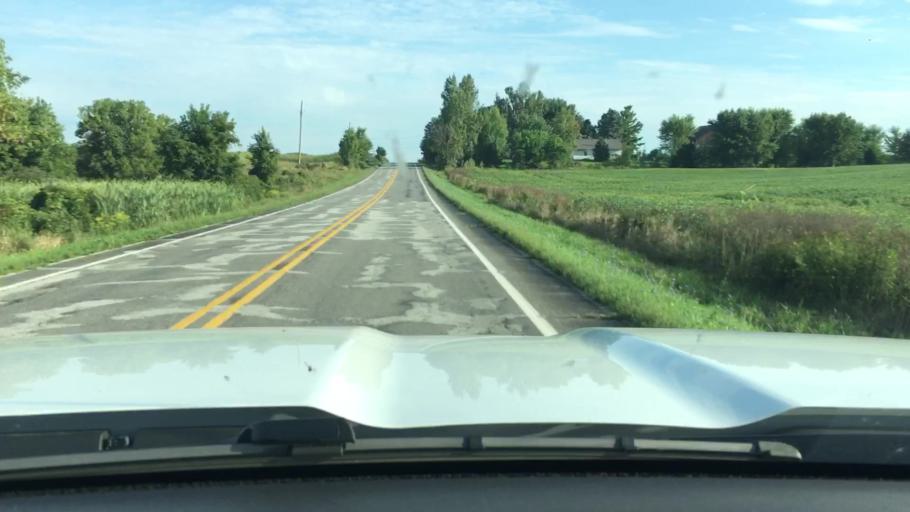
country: US
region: Michigan
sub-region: Kent County
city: Kent City
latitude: 43.2131
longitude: -85.7709
